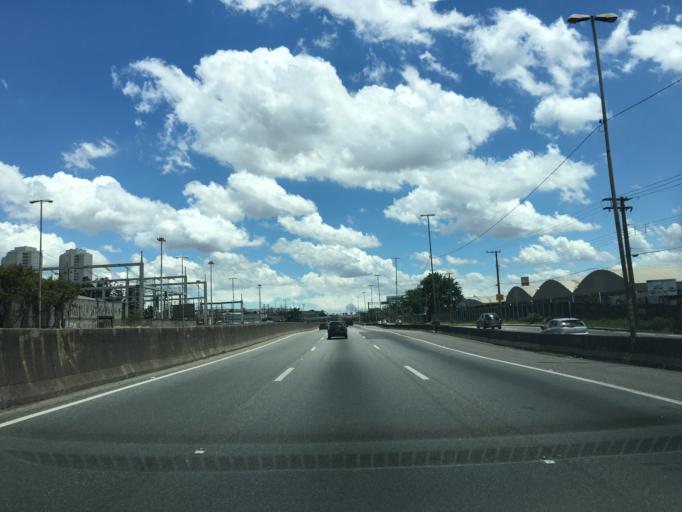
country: BR
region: Sao Paulo
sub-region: Guarulhos
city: Guarulhos
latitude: -23.4800
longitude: -46.5601
